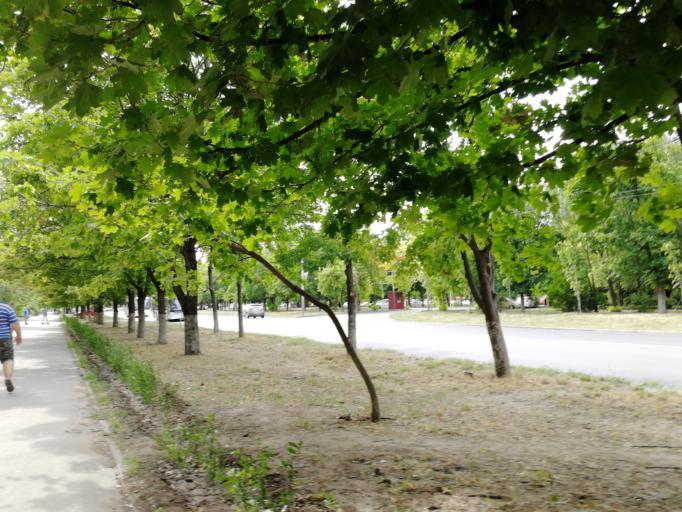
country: RU
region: Rostov
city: Rostov-na-Donu
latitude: 47.2122
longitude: 39.6296
